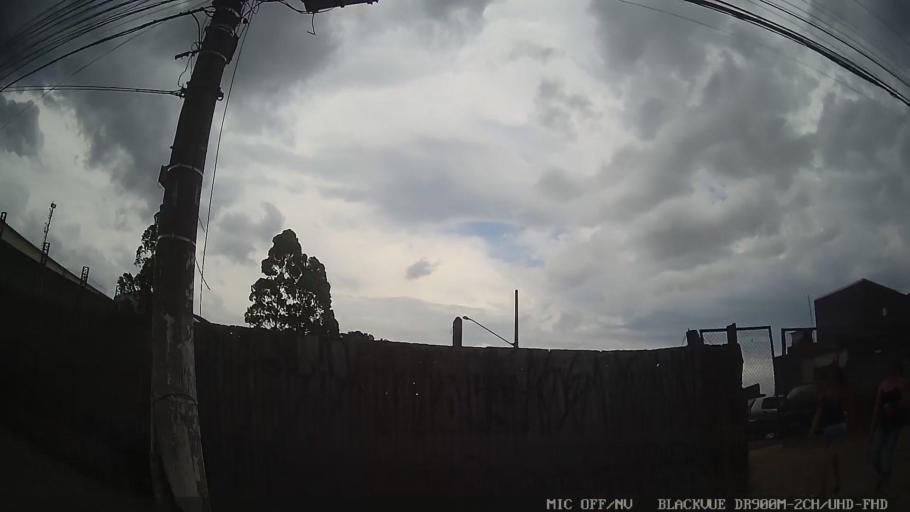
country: BR
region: Sao Paulo
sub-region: Itaquaquecetuba
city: Itaquaquecetuba
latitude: -23.4635
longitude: -46.3247
